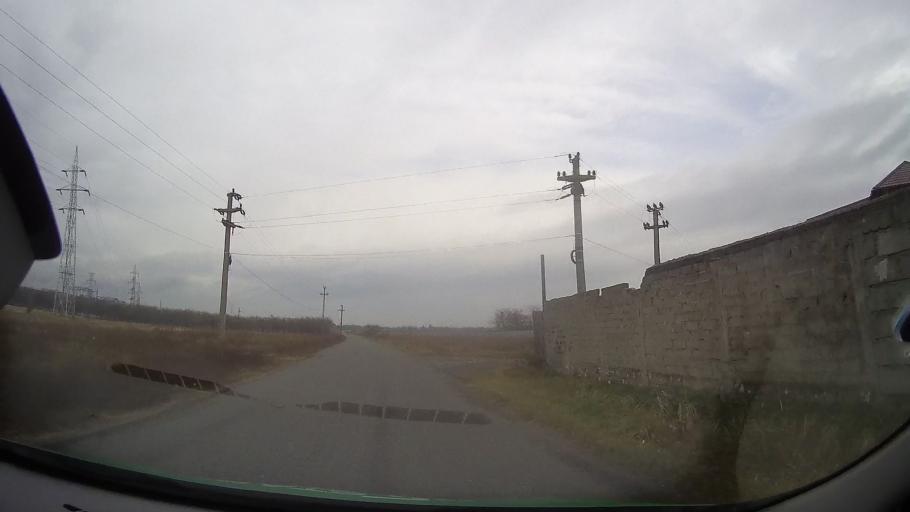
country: RO
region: Prahova
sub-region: Comuna Berceni
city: Berceni
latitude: 44.9376
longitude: 26.1197
